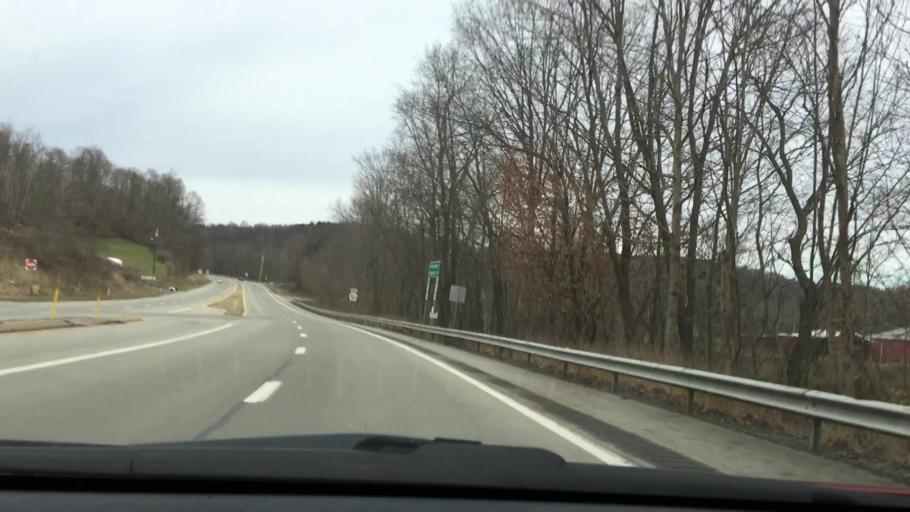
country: US
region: Pennsylvania
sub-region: Fayette County
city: Perryopolis
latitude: 40.0011
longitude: -79.7614
